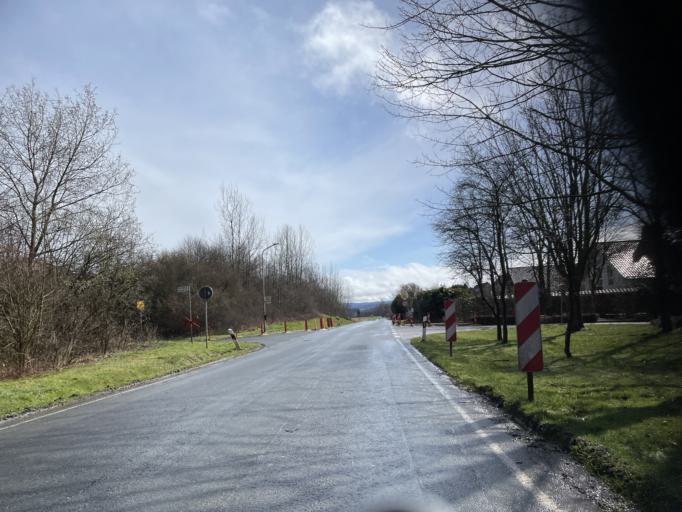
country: DE
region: North Rhine-Westphalia
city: Porta Westfalica
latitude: 52.2320
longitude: 8.9421
